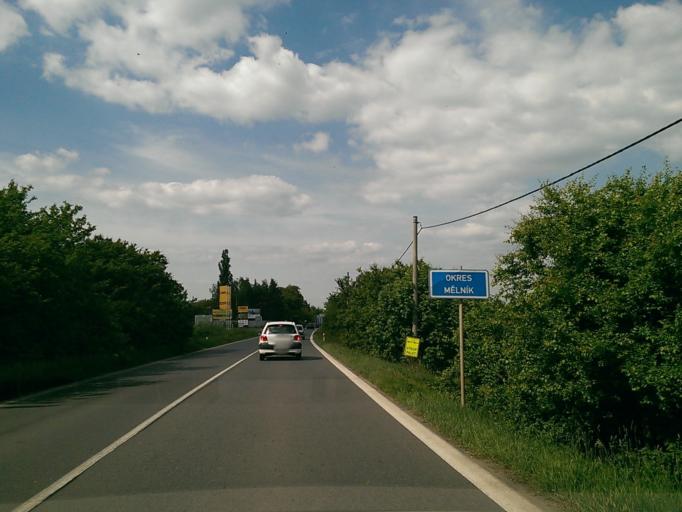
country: CZ
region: Central Bohemia
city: Libeznice
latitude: 50.2271
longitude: 14.4947
